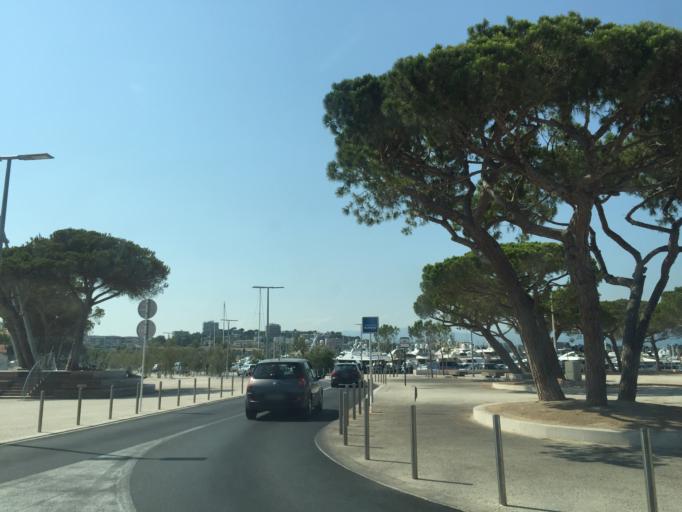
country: FR
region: Provence-Alpes-Cote d'Azur
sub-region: Departement des Alpes-Maritimes
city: Antibes
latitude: 43.5835
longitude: 7.1275
